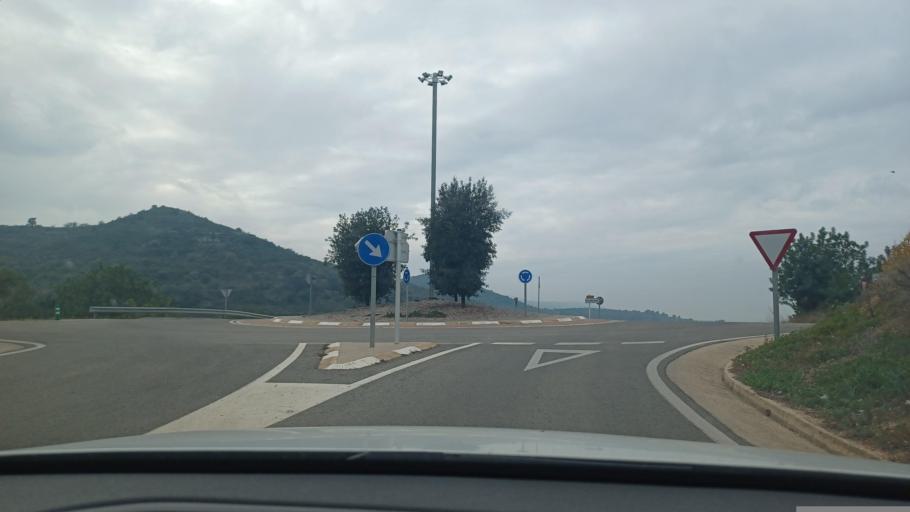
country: ES
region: Catalonia
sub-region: Provincia de Tarragona
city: Ulldecona
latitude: 40.6511
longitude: 0.4667
